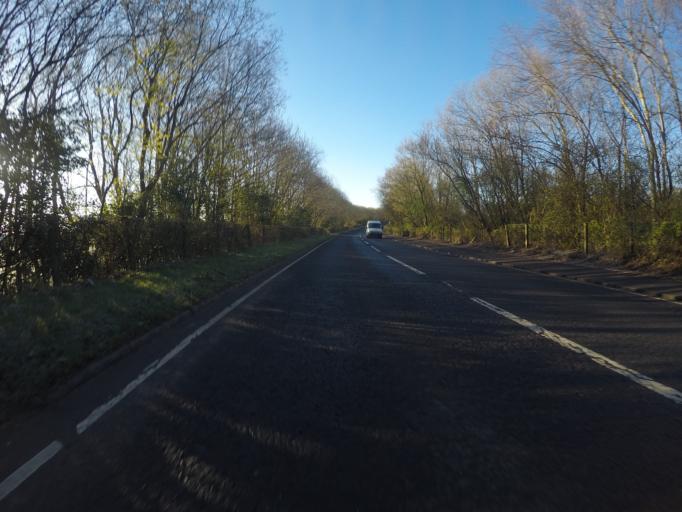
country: GB
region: Scotland
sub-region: North Ayrshire
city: Stevenston
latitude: 55.6402
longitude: -4.7408
